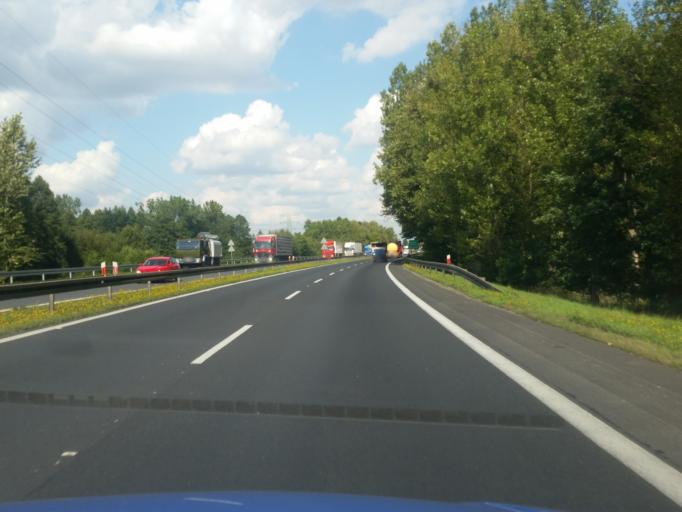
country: PL
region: Silesian Voivodeship
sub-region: Powiat czestochowski
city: Kamienica Polska
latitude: 50.6719
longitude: 19.1231
